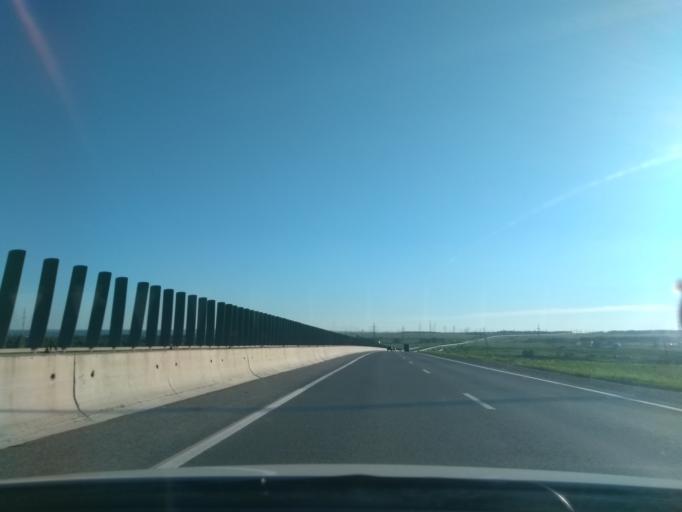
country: RU
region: Perm
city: Ferma
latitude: 57.9343
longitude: 56.3537
